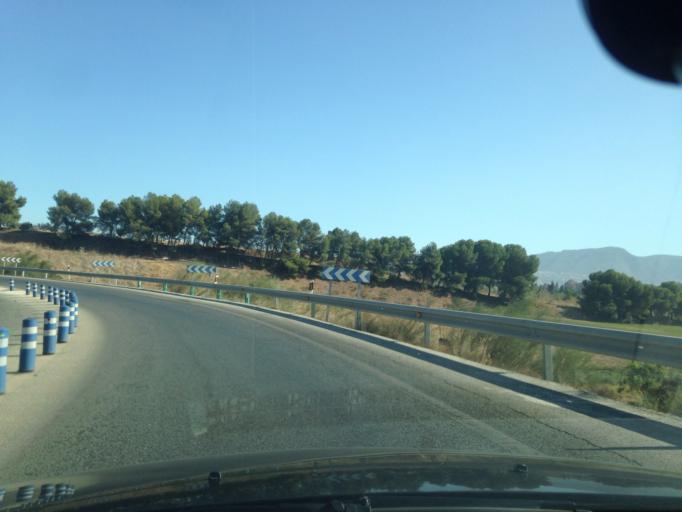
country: ES
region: Andalusia
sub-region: Provincia de Malaga
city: Alhaurin de la Torre
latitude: 36.7151
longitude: -4.5554
